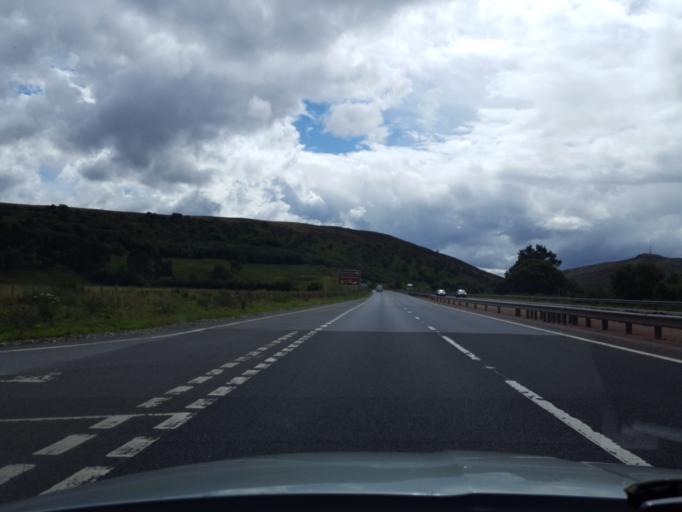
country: GB
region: Scotland
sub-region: Highland
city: Kingussie
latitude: 57.0080
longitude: -4.1672
